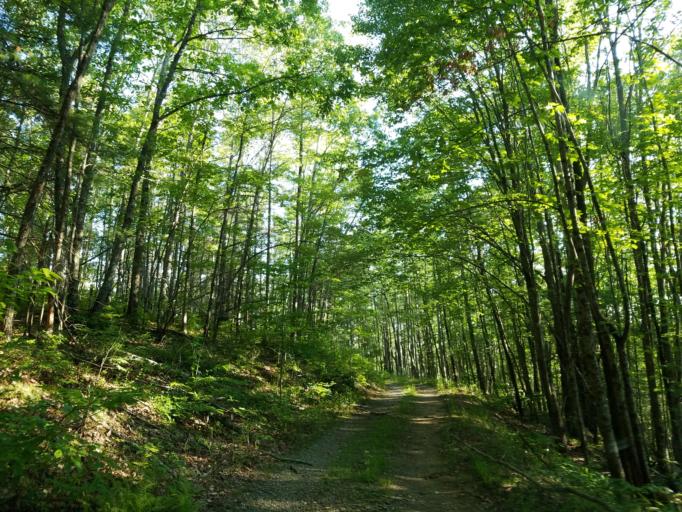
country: US
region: Georgia
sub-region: Fannin County
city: Blue Ridge
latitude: 34.8079
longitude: -84.1652
